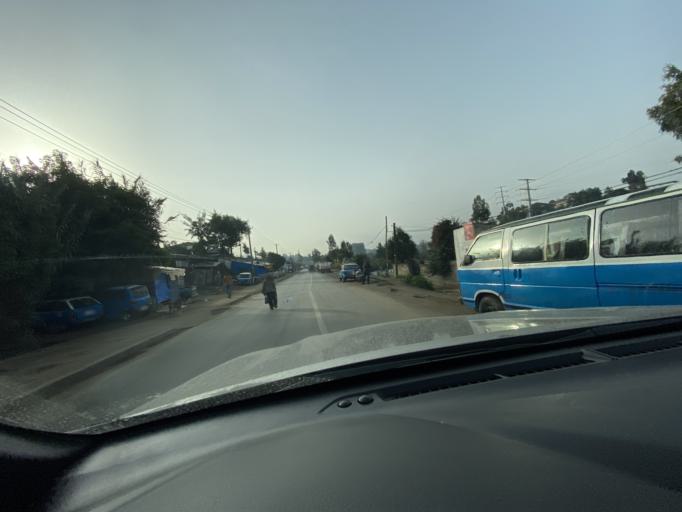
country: ET
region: Adis Abeba
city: Addis Ababa
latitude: 9.0201
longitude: 38.7232
